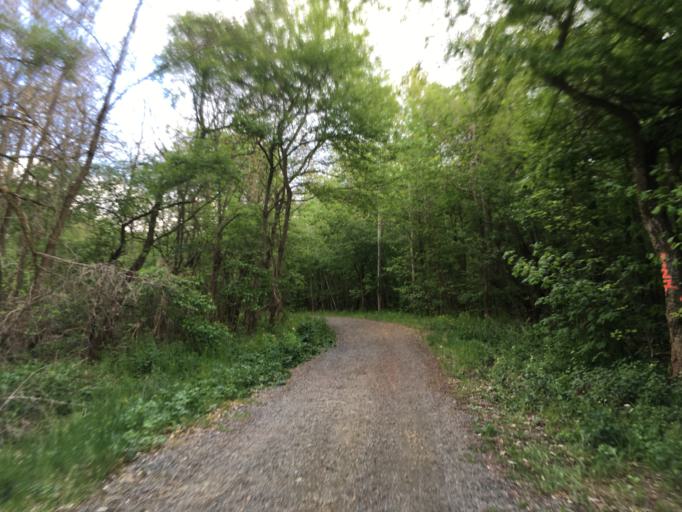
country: DE
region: Berlin
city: Blankenfelde
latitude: 52.6417
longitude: 13.3968
